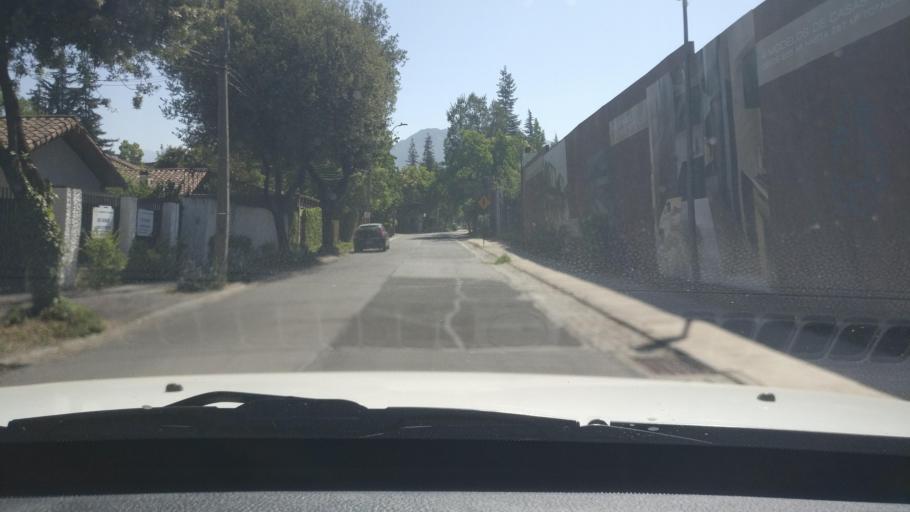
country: CL
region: Santiago Metropolitan
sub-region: Provincia de Santiago
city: Villa Presidente Frei, Nunoa, Santiago, Chile
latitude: -33.3754
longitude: -70.5140
